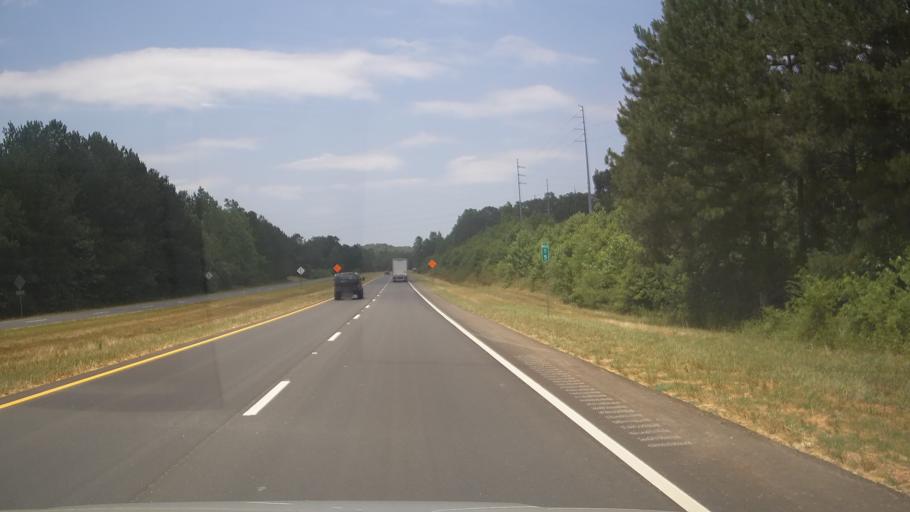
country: US
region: Georgia
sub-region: Jackson County
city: Commerce
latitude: 34.2193
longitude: -83.4461
